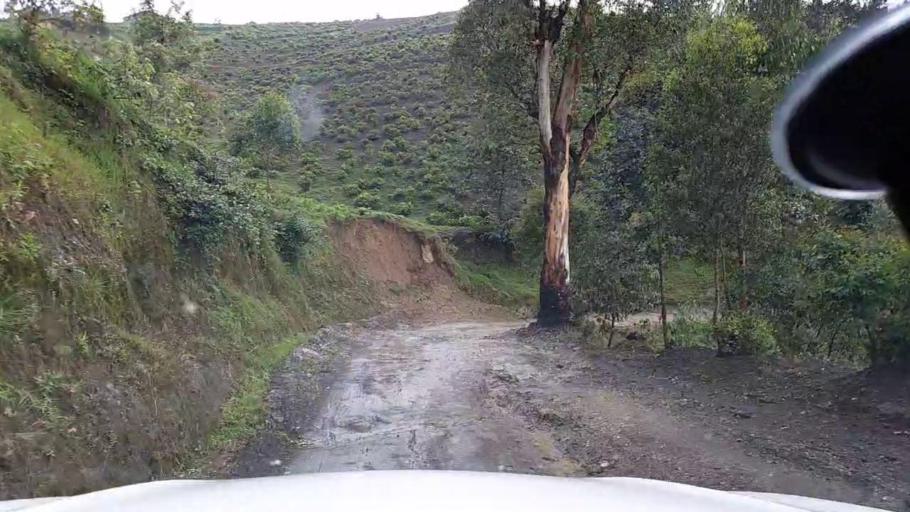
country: RW
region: Western Province
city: Kibuye
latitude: -2.0813
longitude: 29.5132
